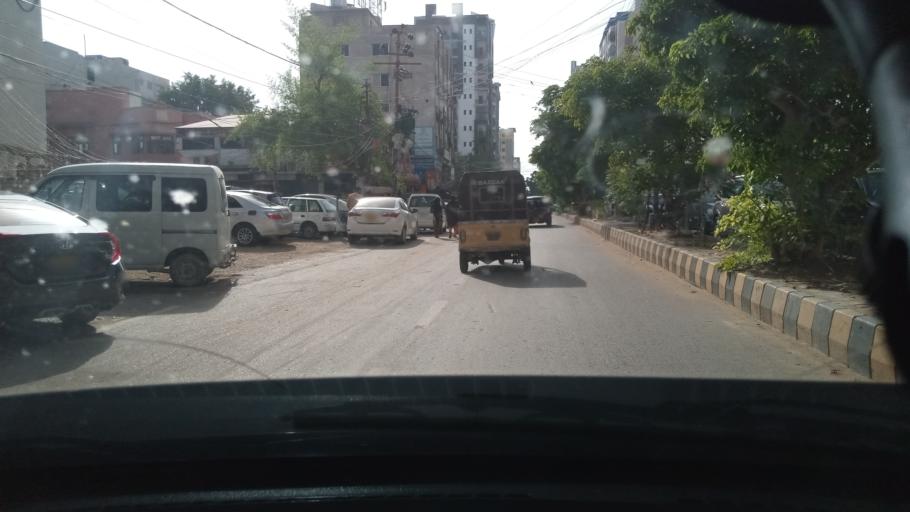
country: PK
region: Sindh
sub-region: Karachi District
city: Karachi
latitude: 24.8731
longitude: 67.0574
